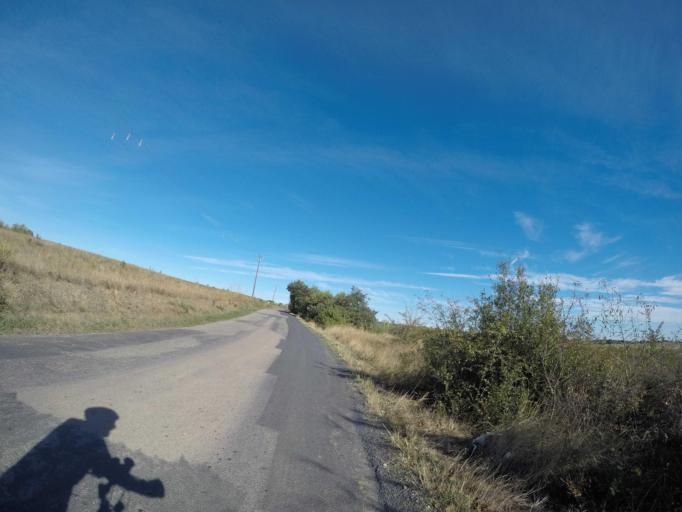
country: FR
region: Languedoc-Roussillon
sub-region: Departement des Pyrenees-Orientales
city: Trouillas
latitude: 42.5972
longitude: 2.8082
